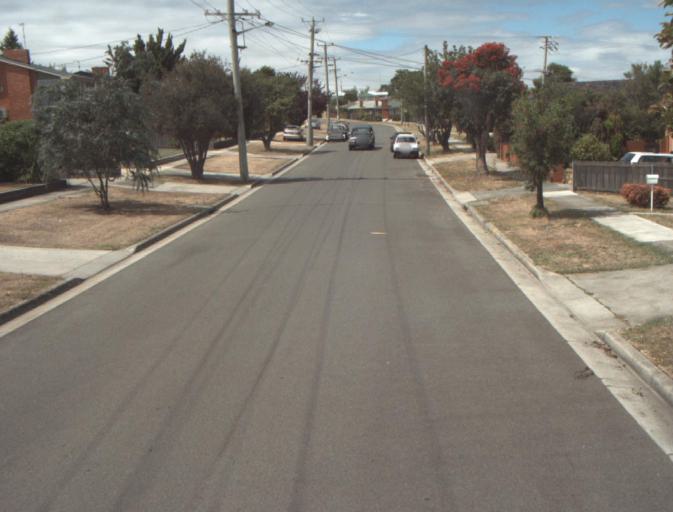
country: AU
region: Tasmania
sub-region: Launceston
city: Mayfield
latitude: -41.3846
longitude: 147.1205
